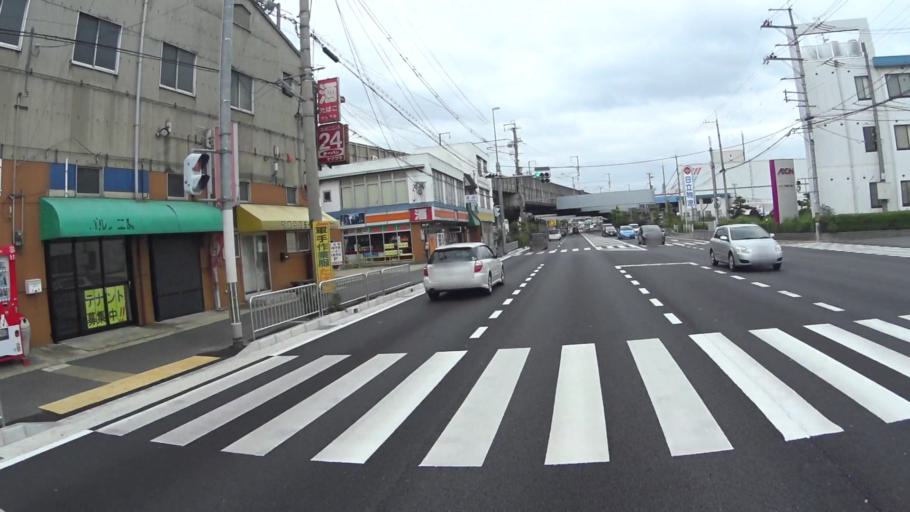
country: JP
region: Kyoto
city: Yawata
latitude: 34.8973
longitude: 135.6882
